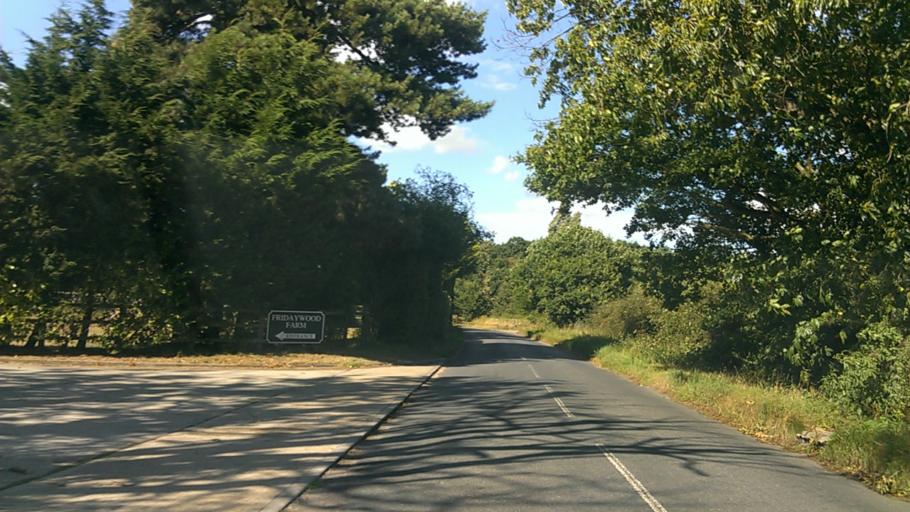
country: GB
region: England
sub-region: Essex
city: Layer de la Haye
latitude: 51.8530
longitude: 0.8828
